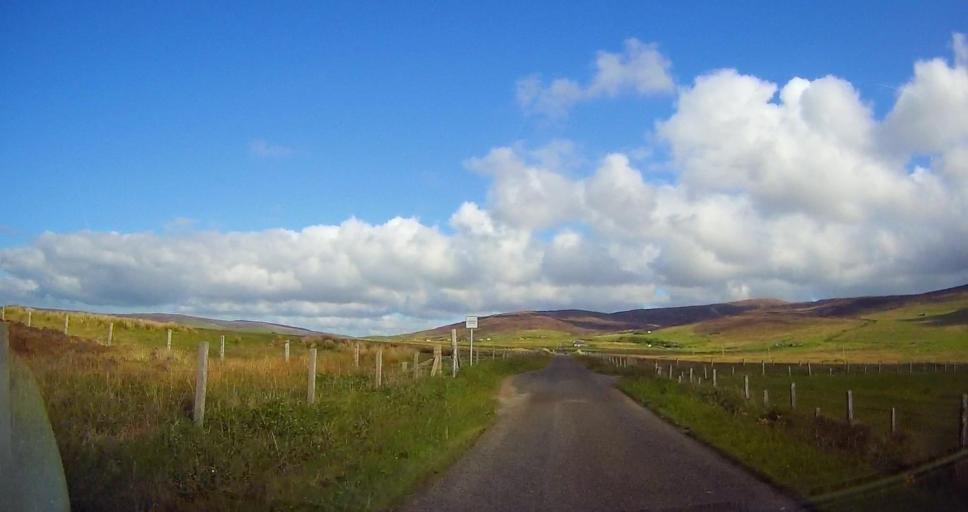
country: GB
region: Scotland
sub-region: Orkney Islands
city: Stromness
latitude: 58.9836
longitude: -3.1868
